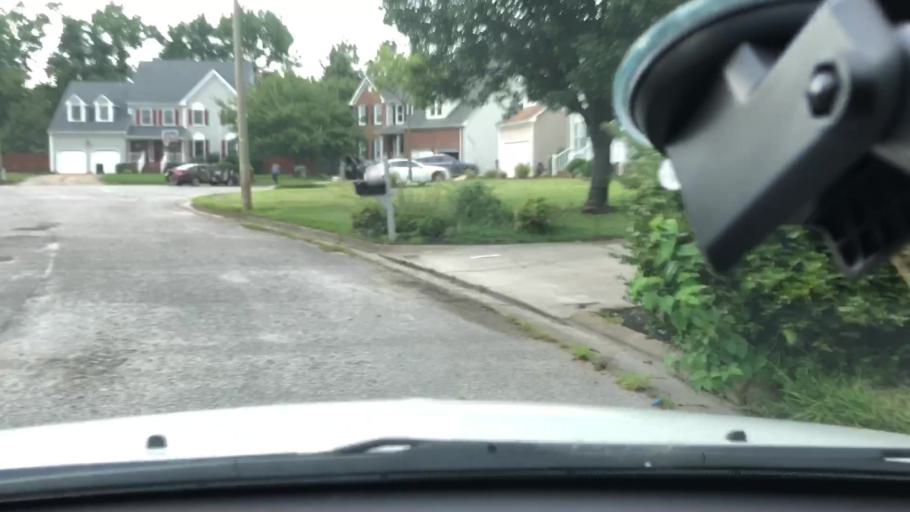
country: US
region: Virginia
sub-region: City of Chesapeake
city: Chesapeake
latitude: 36.7167
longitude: -76.2719
